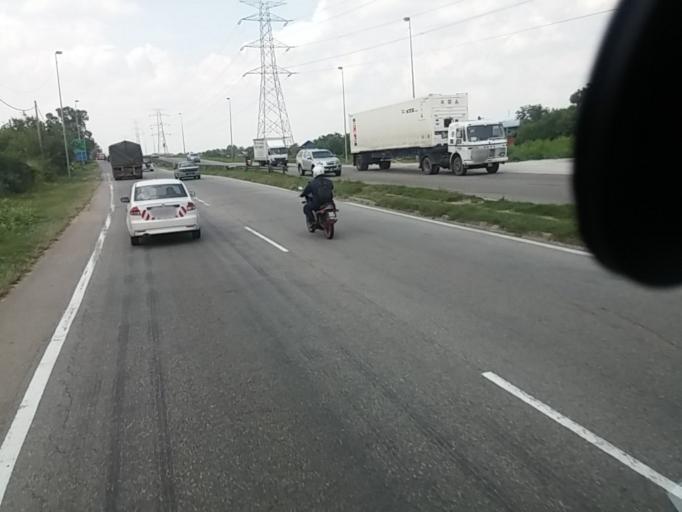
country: MY
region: Selangor
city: Klang
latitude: 2.9779
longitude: 101.3980
